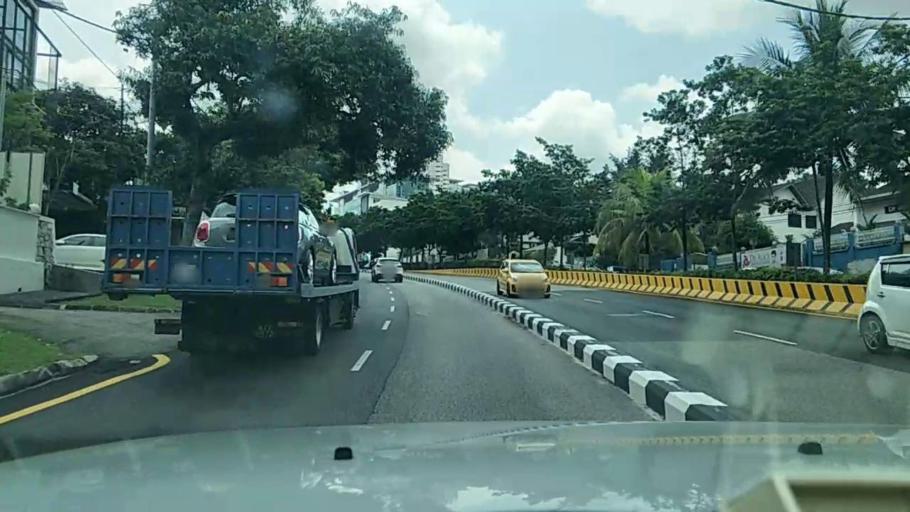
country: MY
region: Kuala Lumpur
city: Kuala Lumpur
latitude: 3.1421
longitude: 101.6710
